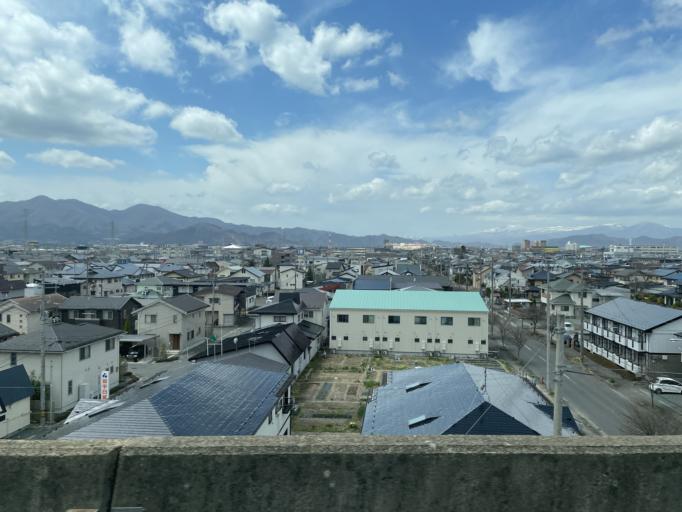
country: JP
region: Iwate
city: Morioka-shi
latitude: 39.6819
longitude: 141.1486
